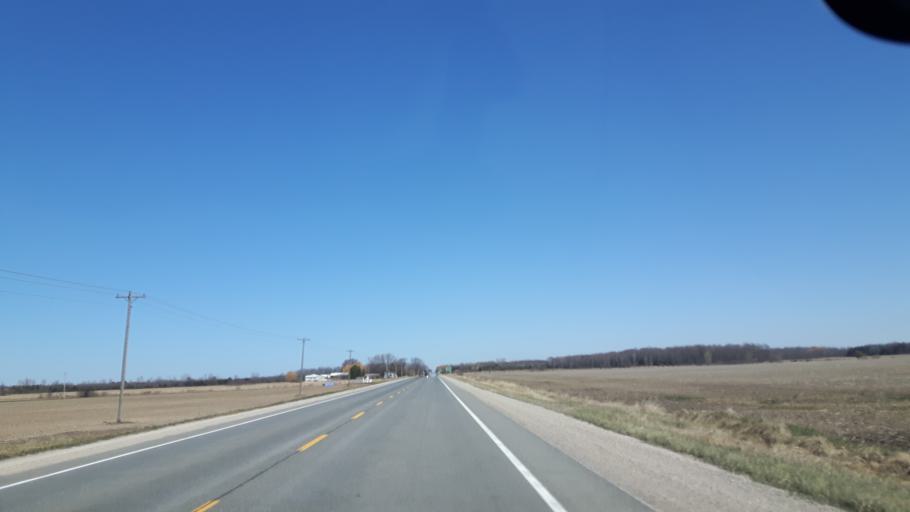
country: CA
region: Ontario
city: Goderich
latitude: 43.6365
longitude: -81.7057
